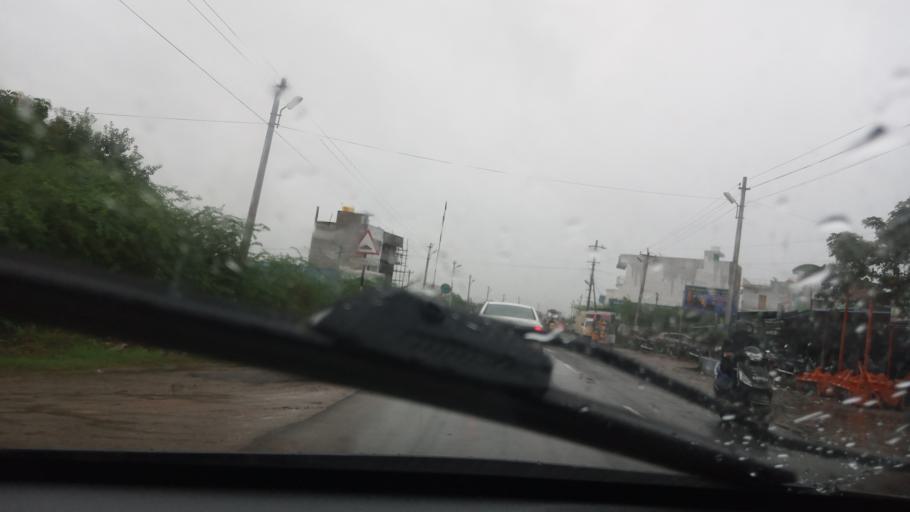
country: IN
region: Tamil Nadu
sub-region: Tiruvannamalai
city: Cheyyar
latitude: 12.6545
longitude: 79.5379
